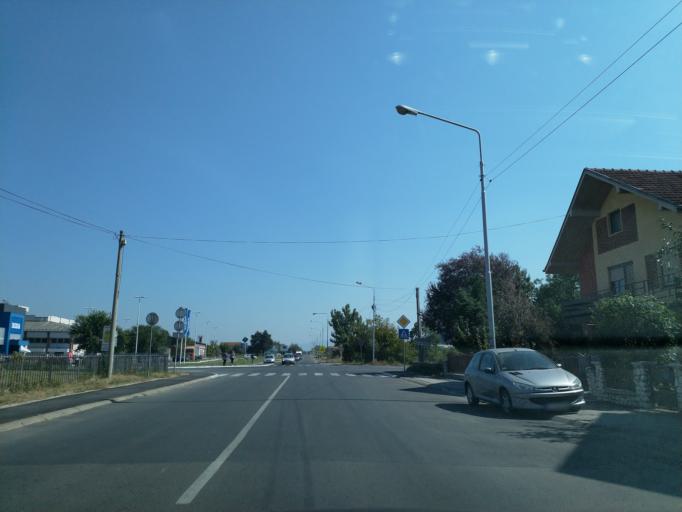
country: RS
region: Central Serbia
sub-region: Rasinski Okrug
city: Trstenik
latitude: 43.6156
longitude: 21.0123
